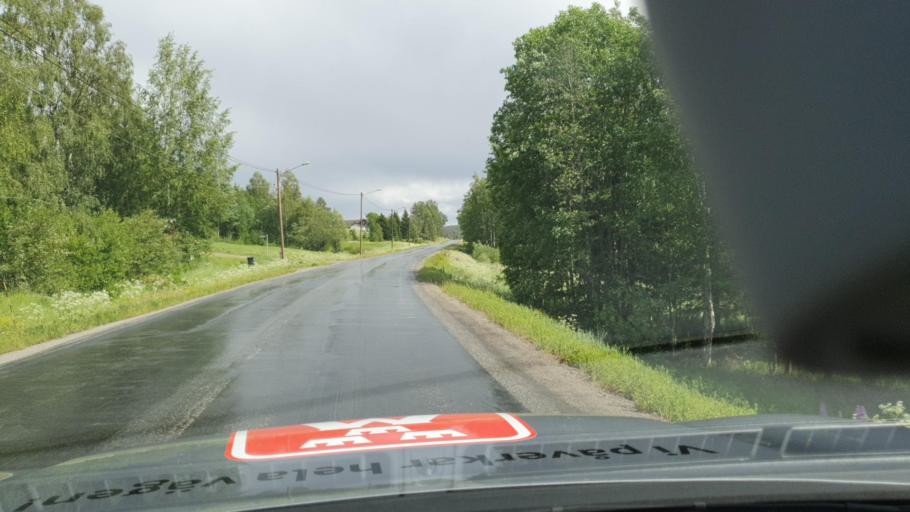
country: SE
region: Vaesternorrland
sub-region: OErnskoeldsviks Kommun
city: Bredbyn
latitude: 63.3302
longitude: 18.2417
